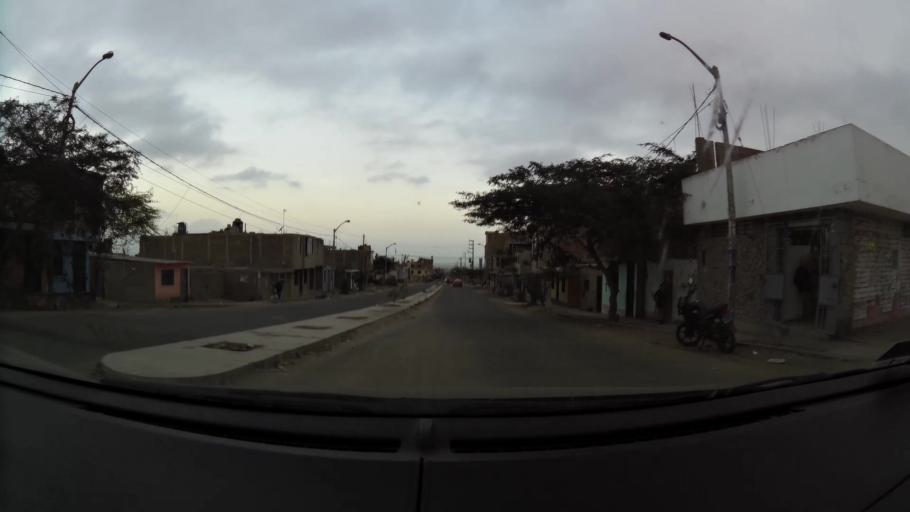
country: PE
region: La Libertad
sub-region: Provincia de Trujillo
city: El Porvenir
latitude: -8.0750
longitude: -79.0205
